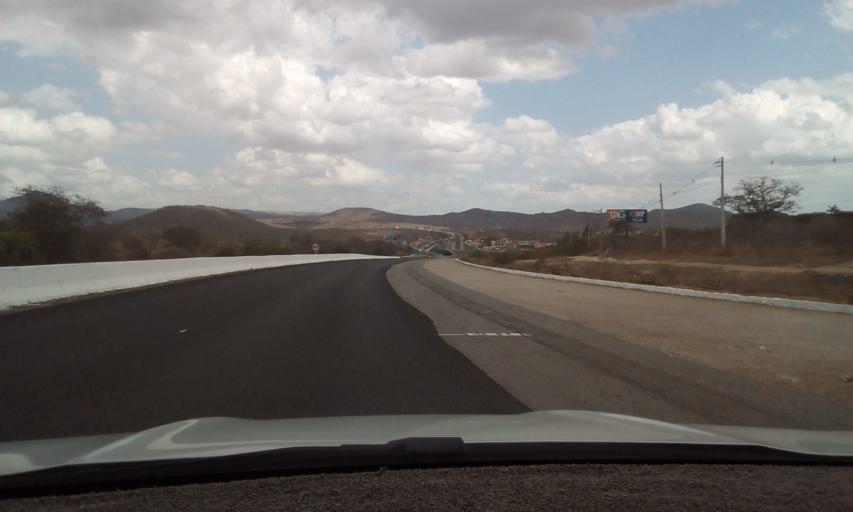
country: BR
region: Pernambuco
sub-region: Toritama
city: Toritama
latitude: -8.1024
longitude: -36.0262
